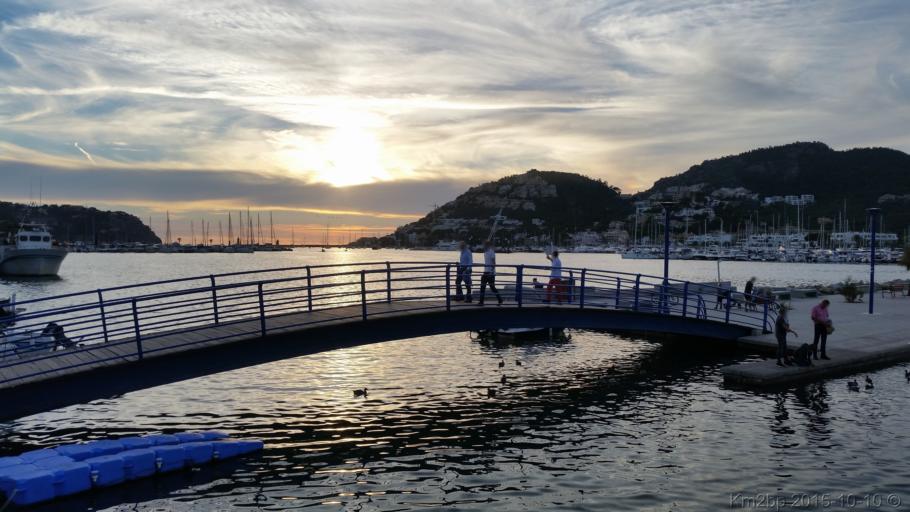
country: ES
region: Balearic Islands
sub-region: Illes Balears
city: Camp de Mar
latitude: 39.5462
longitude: 2.3905
